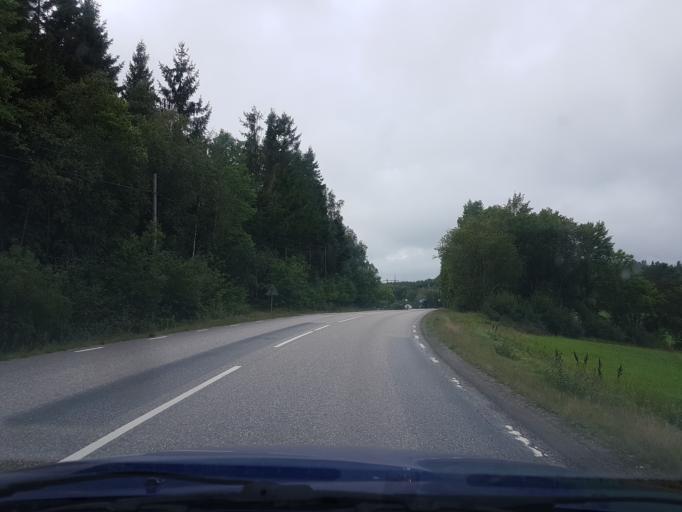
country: SE
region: Vaestra Goetaland
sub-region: Ale Kommun
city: Alvangen
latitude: 57.9444
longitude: 12.1688
